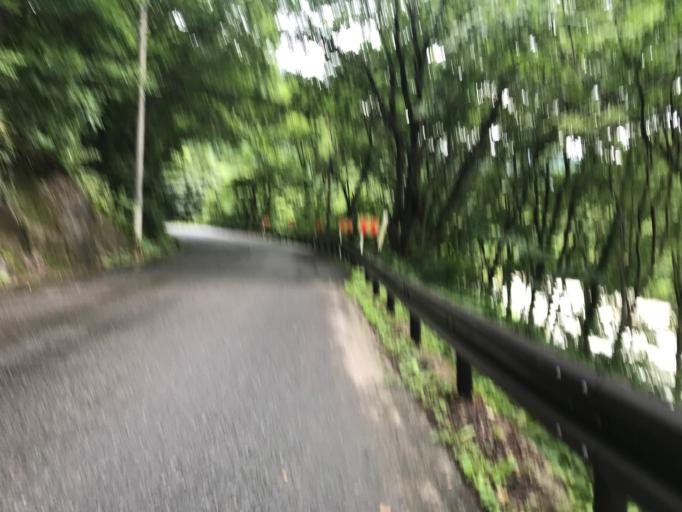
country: JP
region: Gunma
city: Numata
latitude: 36.8183
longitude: 138.9822
